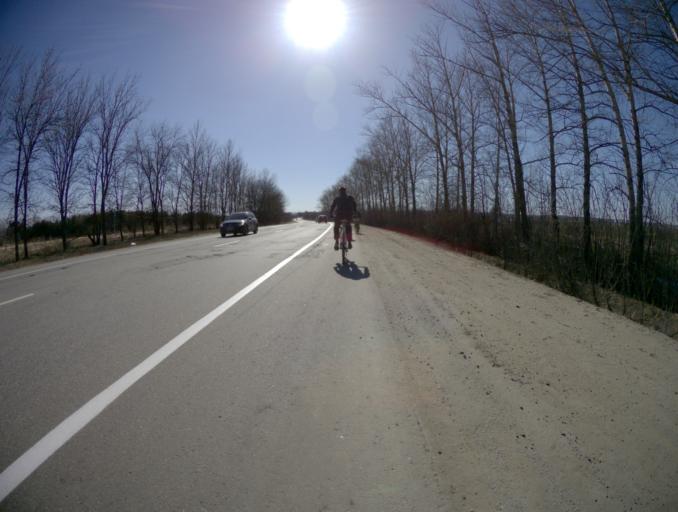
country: RU
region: Vladimir
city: Bogolyubovo
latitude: 56.2087
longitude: 40.5701
